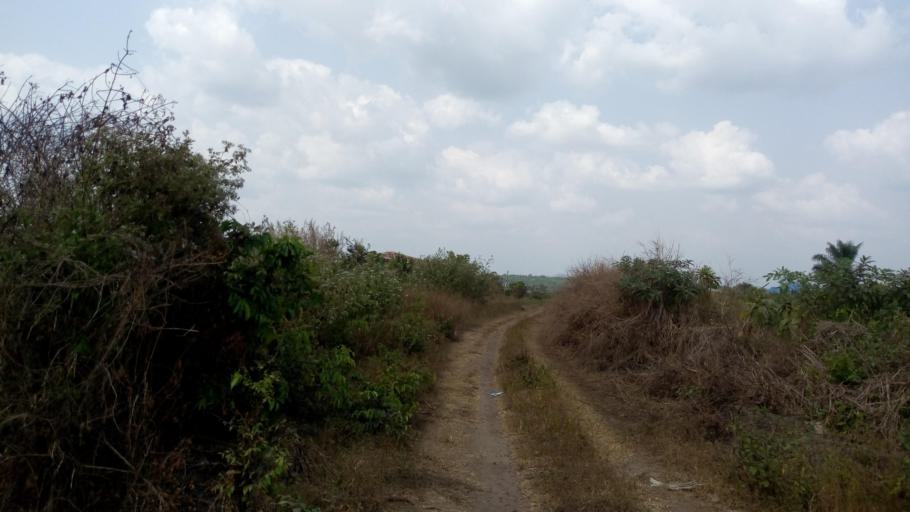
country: SL
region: Southern Province
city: Mogbwemo
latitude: 7.7890
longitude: -12.3085
